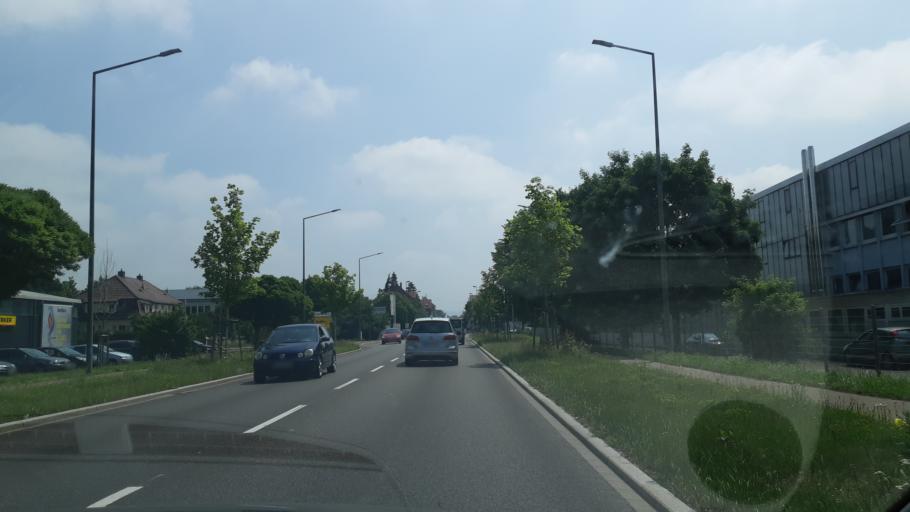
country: DE
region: Baden-Wuerttemberg
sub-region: Regierungsbezirk Stuttgart
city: Eislingen
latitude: 48.6964
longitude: 9.6918
